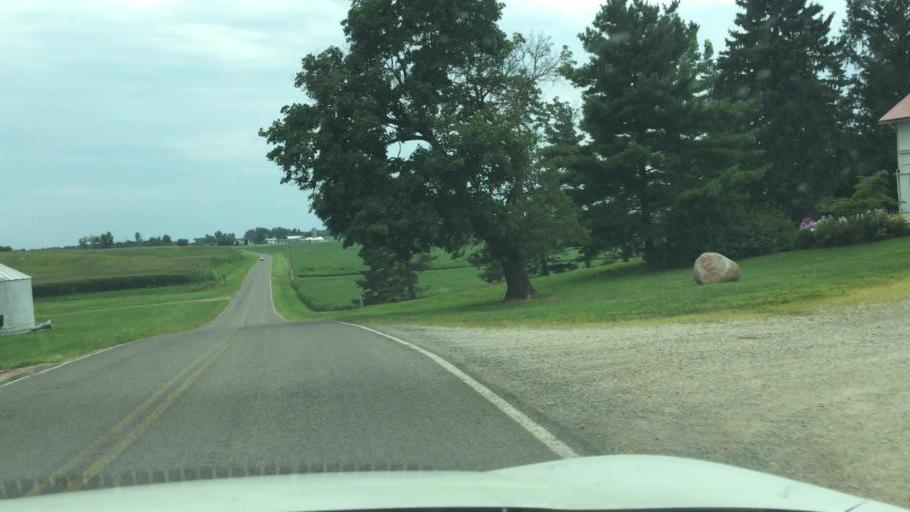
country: US
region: Ohio
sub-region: Champaign County
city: Mechanicsburg
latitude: 40.0661
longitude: -83.6502
